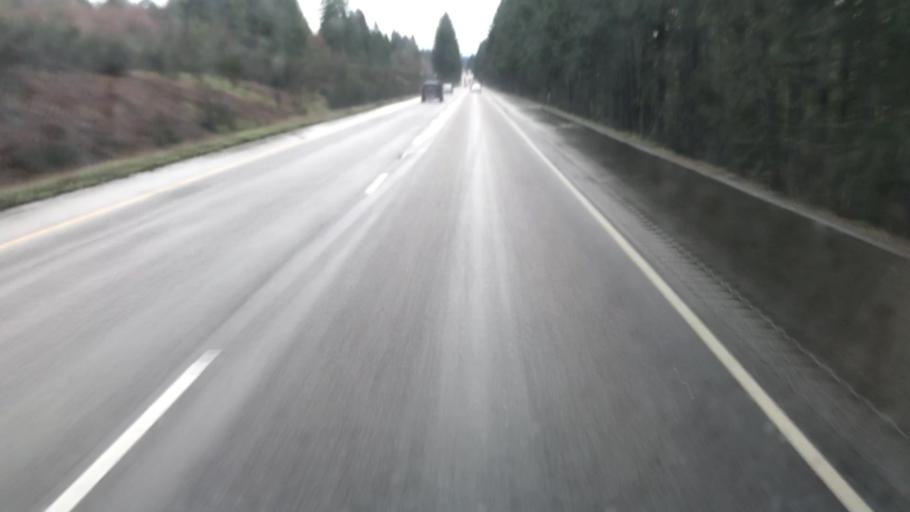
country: US
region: Washington
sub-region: Kitsap County
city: Burley
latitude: 47.4466
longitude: -122.6224
